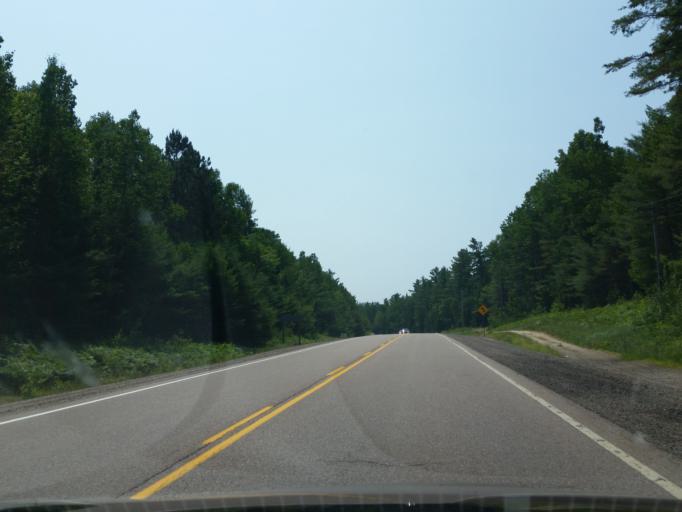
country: CA
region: Ontario
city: Deep River
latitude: 46.1944
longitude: -77.8793
